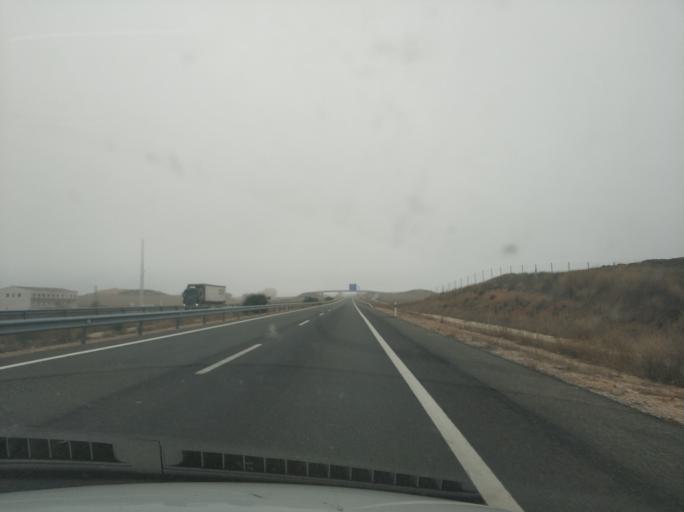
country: ES
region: Castille and Leon
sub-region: Provincia de Soria
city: Adradas
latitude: 41.3606
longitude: -2.4727
